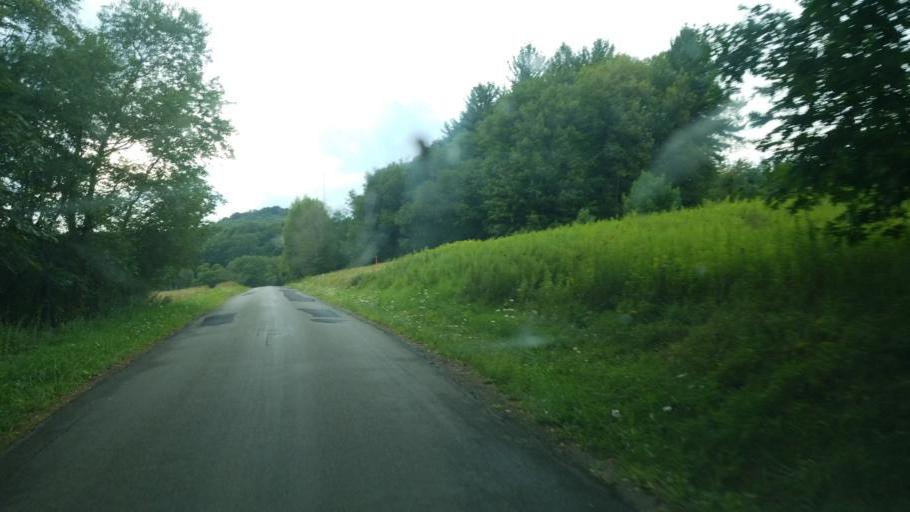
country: US
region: Pennsylvania
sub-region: Clarion County
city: Clarion
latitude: 41.1775
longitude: -79.3816
